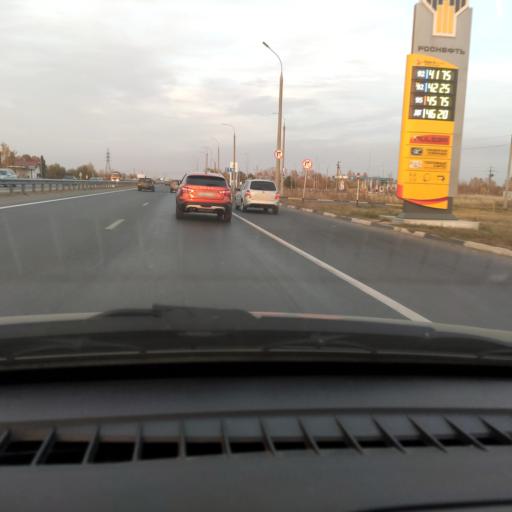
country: RU
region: Samara
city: Tol'yatti
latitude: 53.5581
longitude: 49.3546
